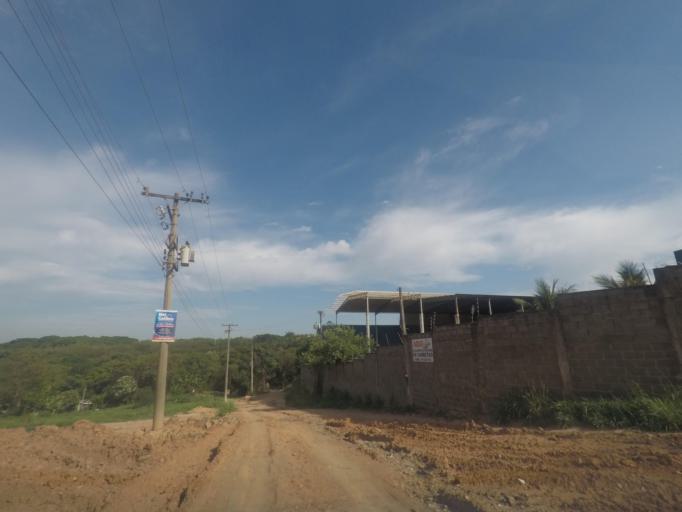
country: BR
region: Sao Paulo
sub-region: Sumare
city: Sumare
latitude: -22.7915
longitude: -47.2317
